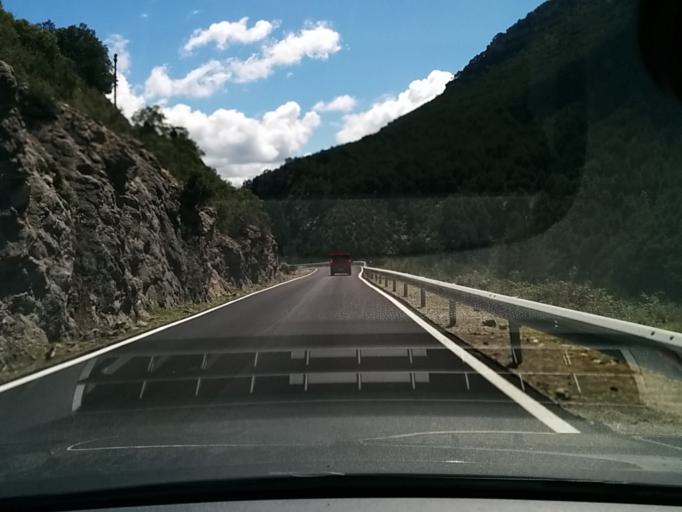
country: ES
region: Aragon
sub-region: Provincia de Huesca
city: Boltana
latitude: 42.4677
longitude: 0.0116
